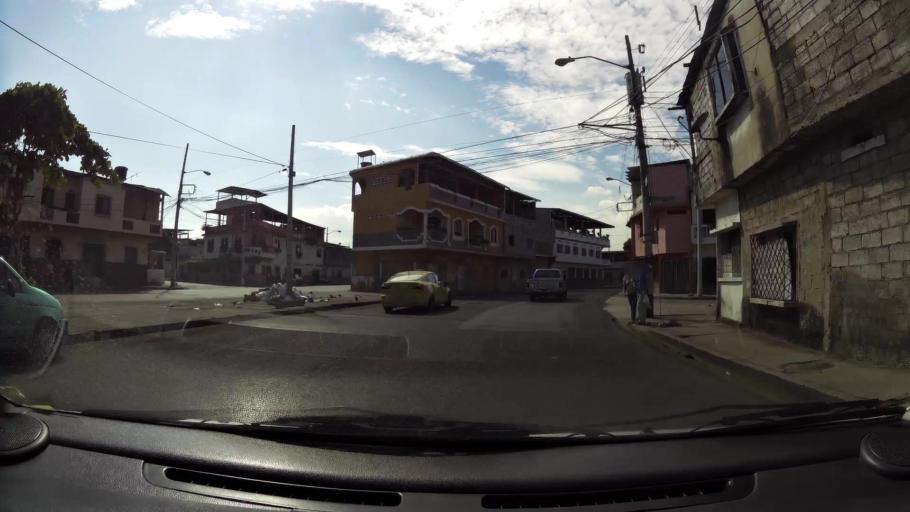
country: EC
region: Guayas
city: Guayaquil
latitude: -2.2201
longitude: -79.9058
